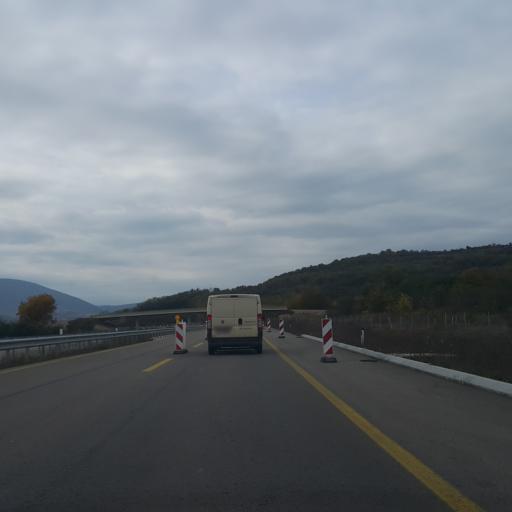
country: RS
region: Central Serbia
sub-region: Pirotski Okrug
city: Bela Palanka
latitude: 43.2353
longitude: 22.3660
